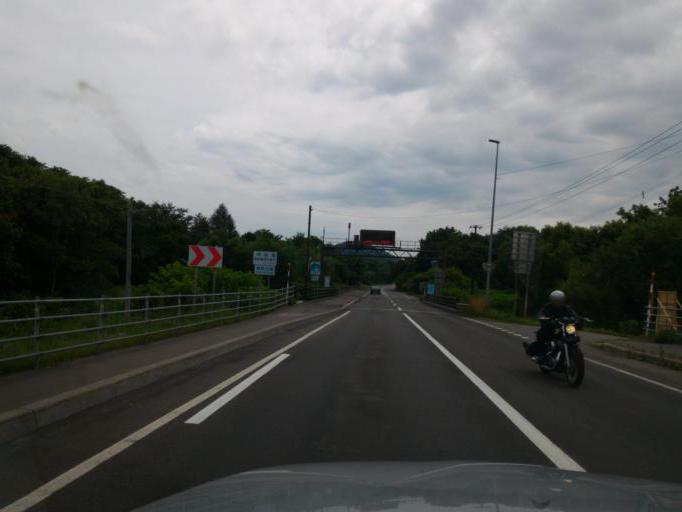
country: JP
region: Hokkaido
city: Nanae
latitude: 42.0006
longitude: 140.6346
